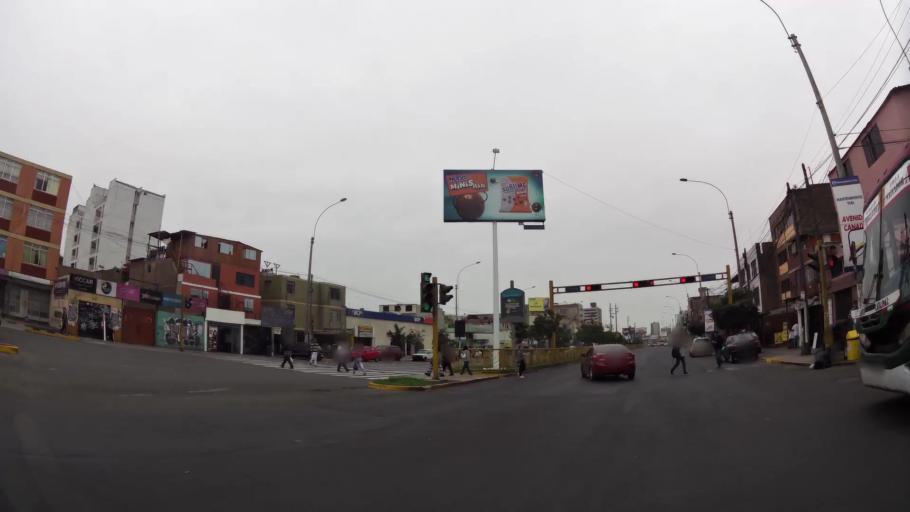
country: PE
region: Lima
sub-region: Lima
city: San Luis
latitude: -12.0816
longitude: -77.0232
